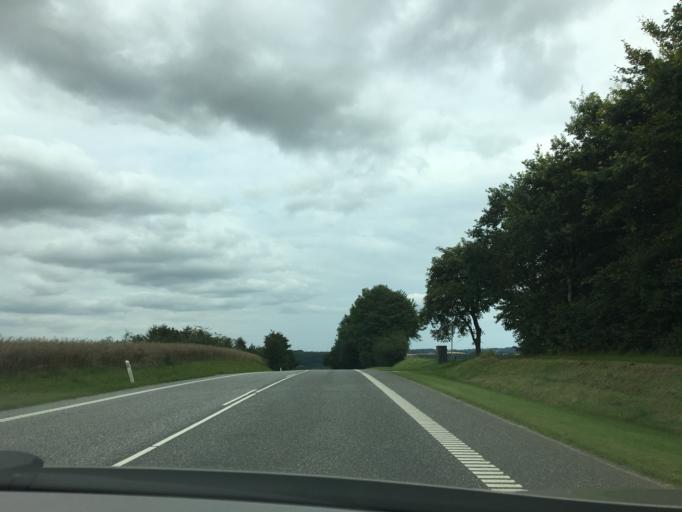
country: DK
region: South Denmark
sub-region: Vejle Kommune
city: Jelling
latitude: 55.7008
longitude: 9.3971
